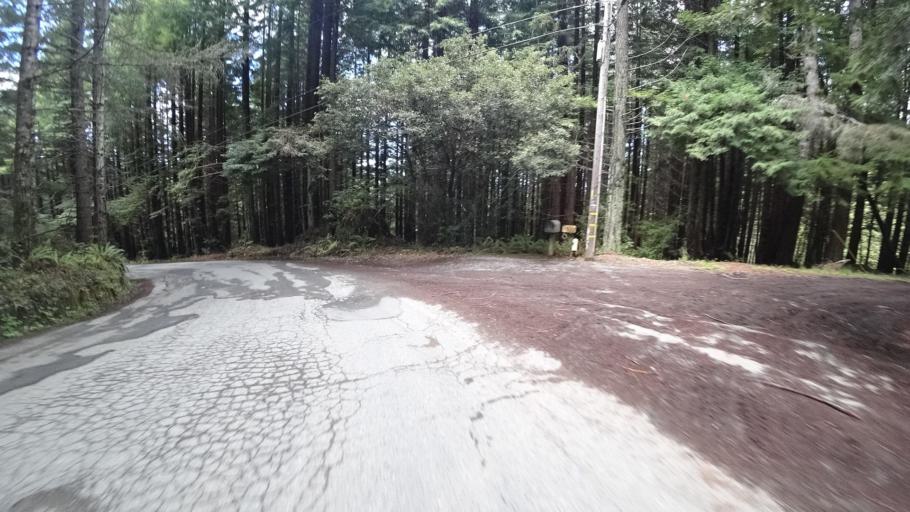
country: US
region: California
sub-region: Humboldt County
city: Blue Lake
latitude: 40.8989
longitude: -123.9982
